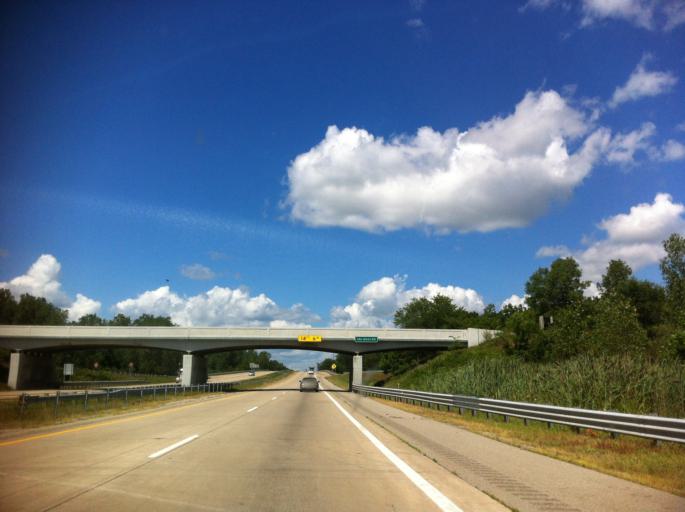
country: US
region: Michigan
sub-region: Monroe County
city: Dundee
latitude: 41.9092
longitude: -83.6618
